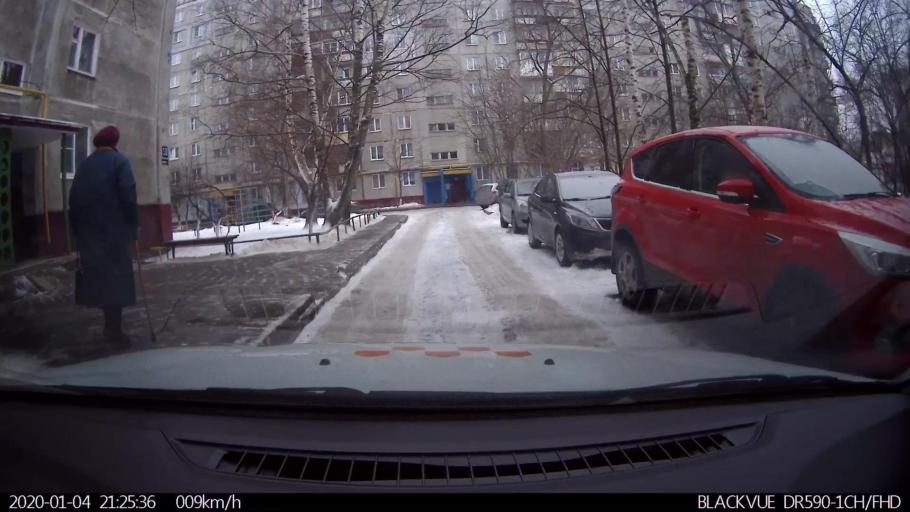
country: RU
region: Nizjnij Novgorod
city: Burevestnik
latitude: 56.2199
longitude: 43.8336
